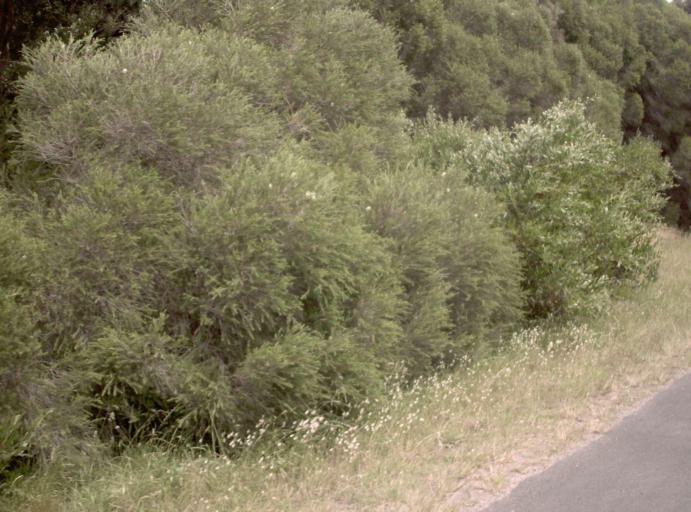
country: AU
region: Victoria
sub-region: Mornington Peninsula
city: Rosebud
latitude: -38.3716
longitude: 144.9040
